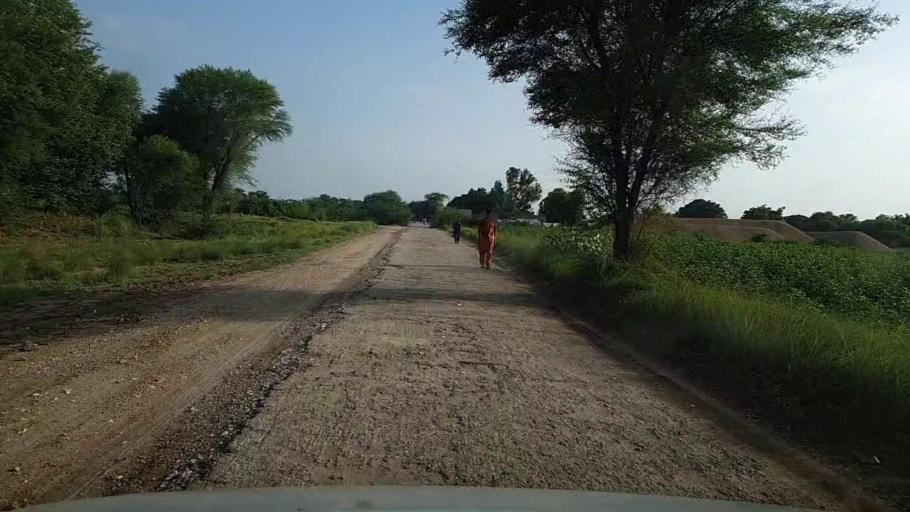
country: PK
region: Sindh
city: Pad Idan
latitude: 26.7994
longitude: 68.2357
